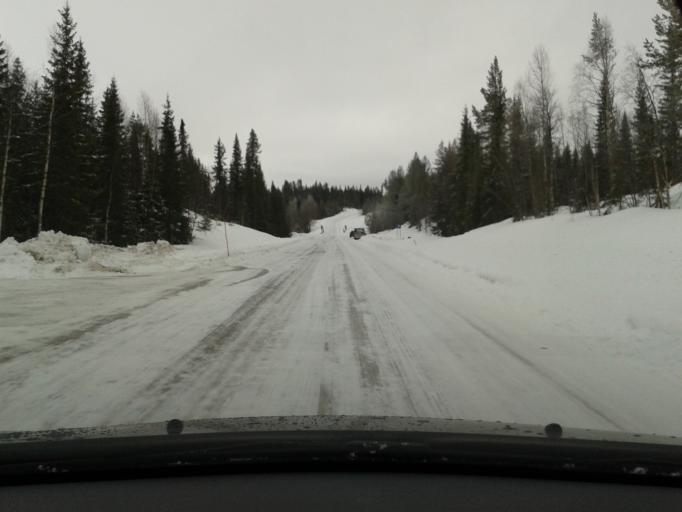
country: SE
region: Vaesterbotten
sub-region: Vilhelmina Kommun
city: Sjoberg
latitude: 64.8239
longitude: 15.9606
